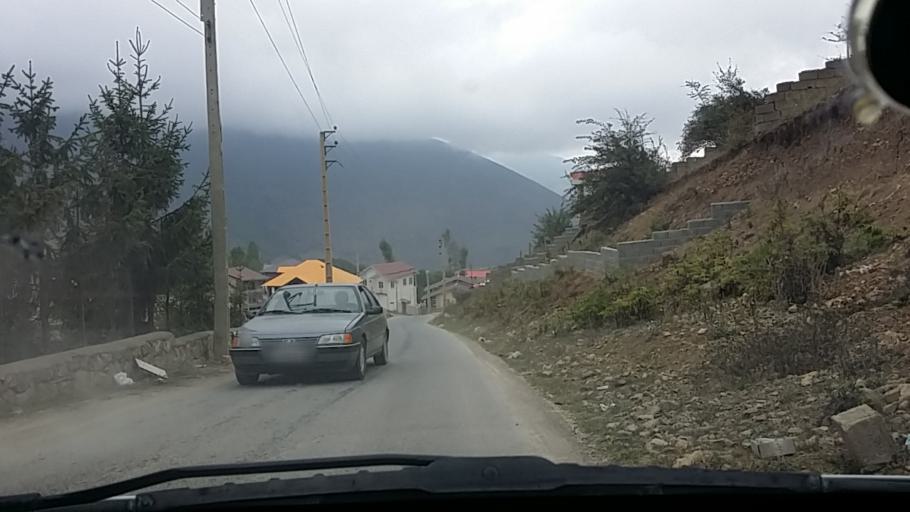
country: IR
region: Mazandaran
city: `Abbasabad
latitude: 36.4768
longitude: 51.1399
